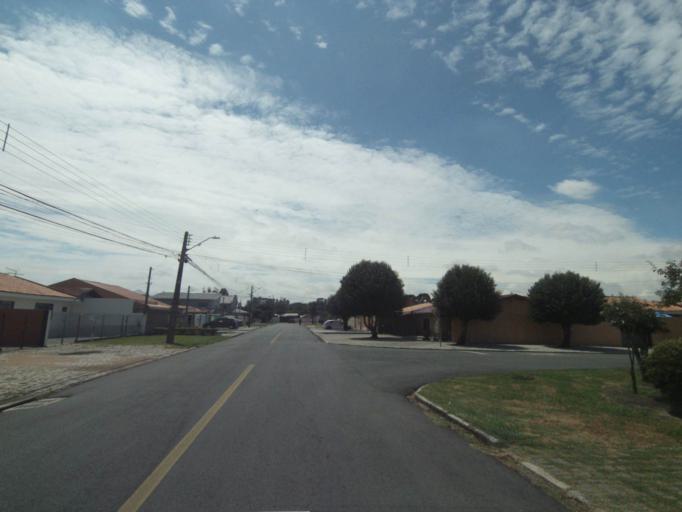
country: BR
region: Parana
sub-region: Pinhais
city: Pinhais
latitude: -25.4741
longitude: -49.1929
